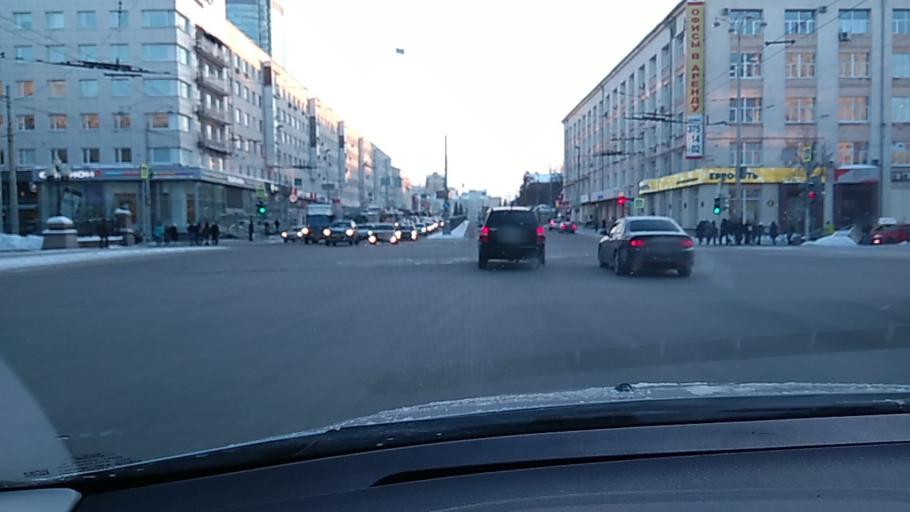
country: RU
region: Sverdlovsk
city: Yekaterinburg
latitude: 56.8402
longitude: 60.6126
